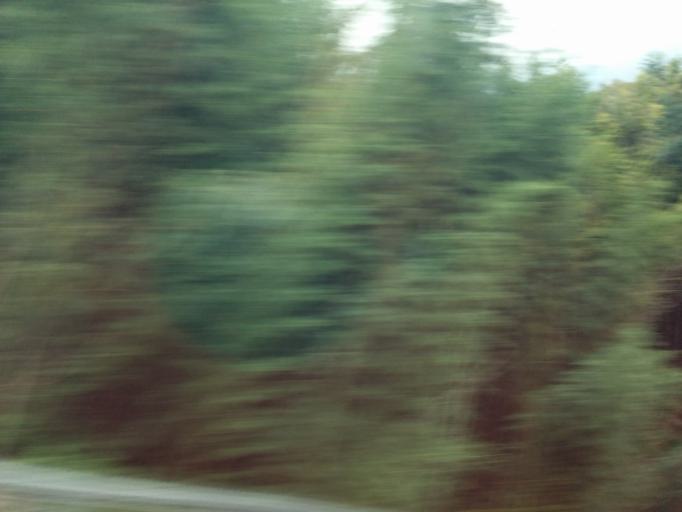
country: JP
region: Shizuoka
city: Numazu
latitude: 35.1449
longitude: 138.7997
